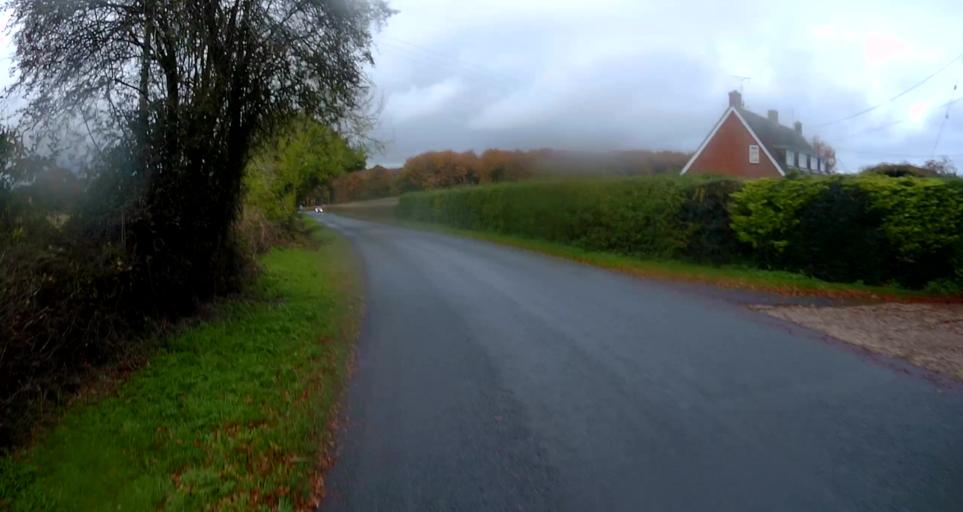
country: GB
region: England
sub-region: Hampshire
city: Four Marks
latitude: 51.1633
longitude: -1.0463
